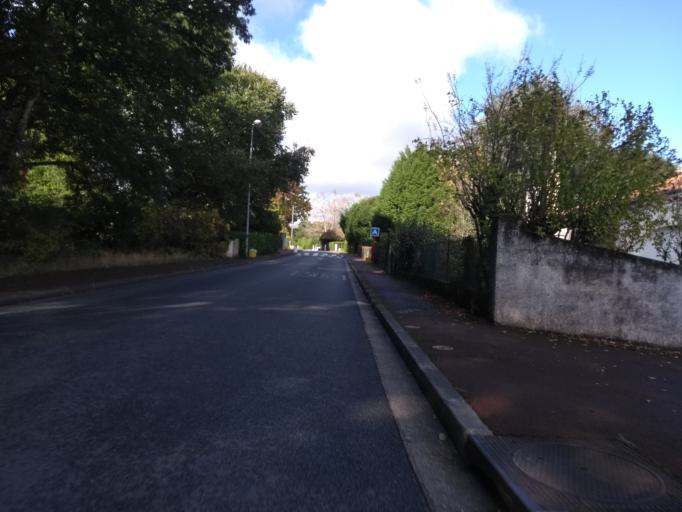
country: FR
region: Aquitaine
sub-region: Departement de la Gironde
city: Canejan
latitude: 44.7686
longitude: -0.6547
